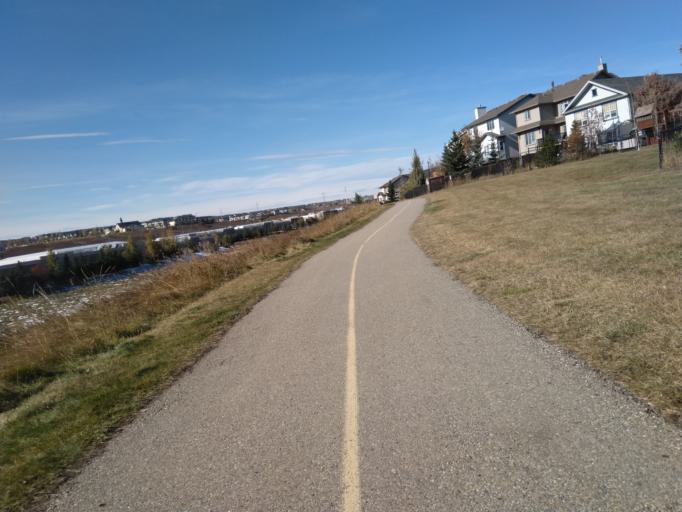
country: CA
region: Alberta
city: Calgary
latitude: 51.1614
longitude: -114.1195
